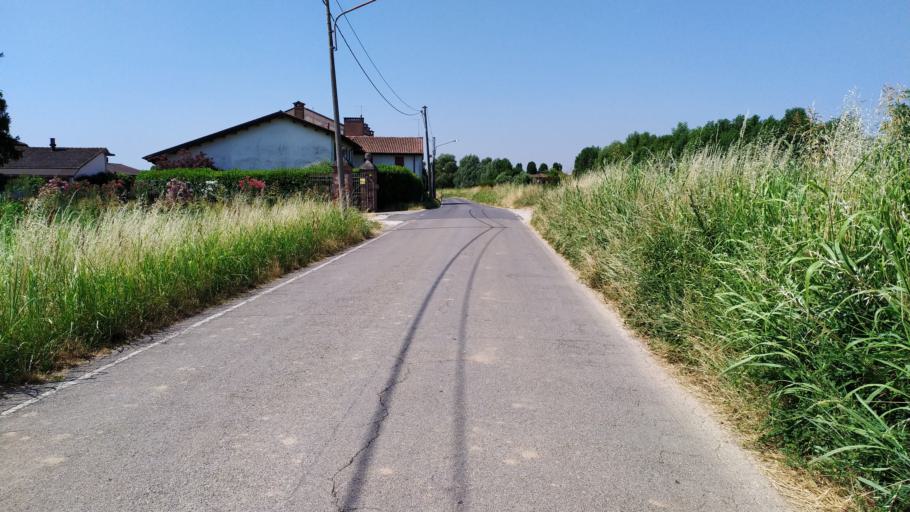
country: IT
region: Veneto
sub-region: Provincia di Vicenza
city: Monticello Conte Otto
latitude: 45.5879
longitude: 11.5377
